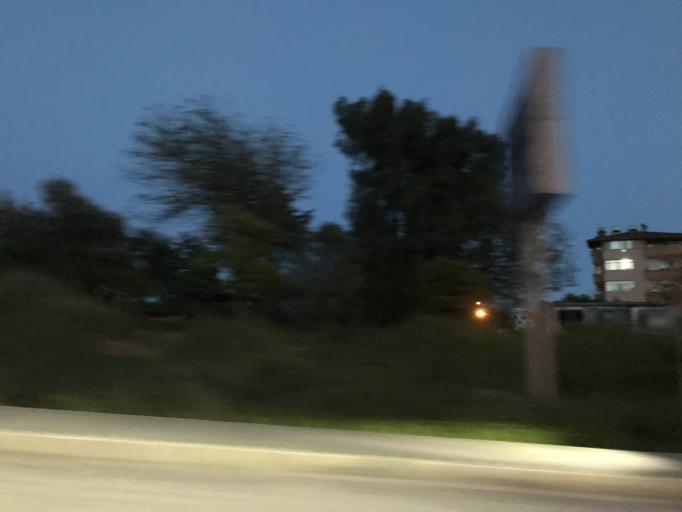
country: TR
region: Hatay
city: Asagiokcular
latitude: 36.1837
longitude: 36.1203
